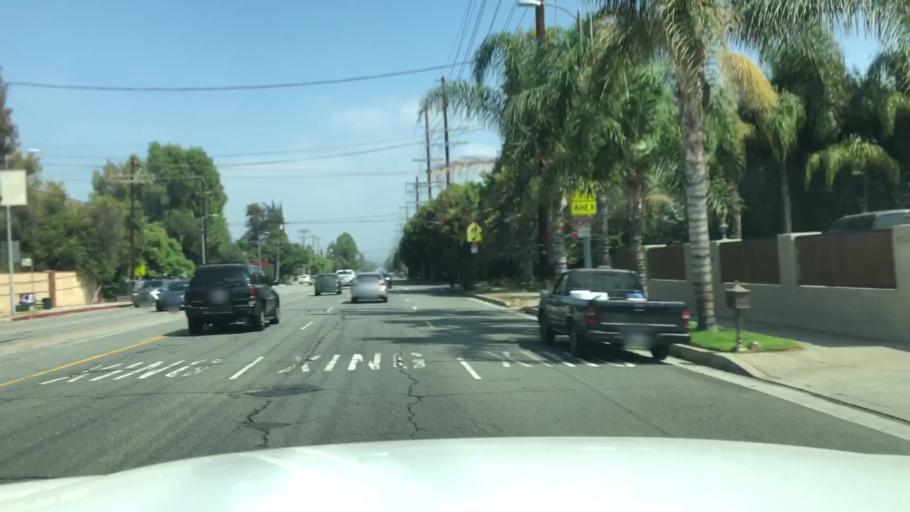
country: US
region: California
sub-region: Los Angeles County
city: Canoga Park
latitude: 34.1751
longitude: -118.5534
